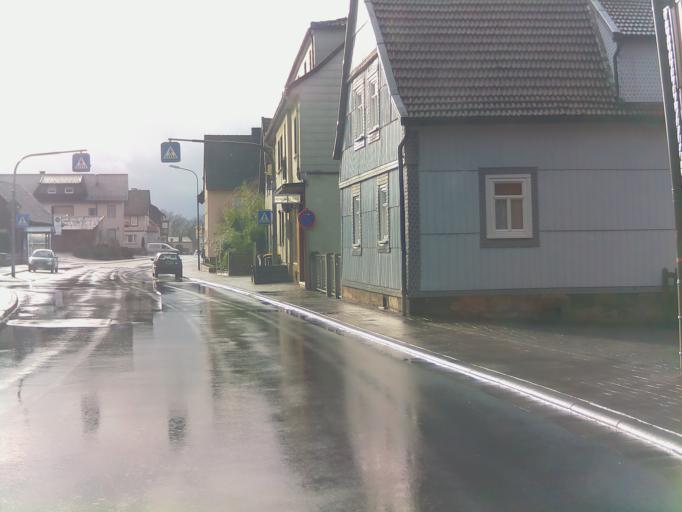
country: DE
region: Hesse
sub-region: Regierungsbezirk Kassel
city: Neuhof
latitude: 50.4503
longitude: 9.6200
